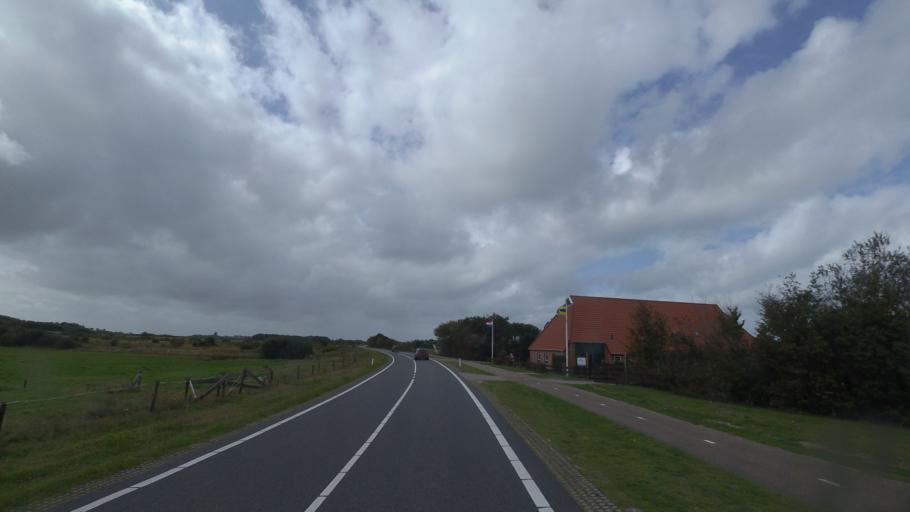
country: NL
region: Friesland
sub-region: Gemeente Ameland
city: Hollum
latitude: 53.4471
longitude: 5.6699
